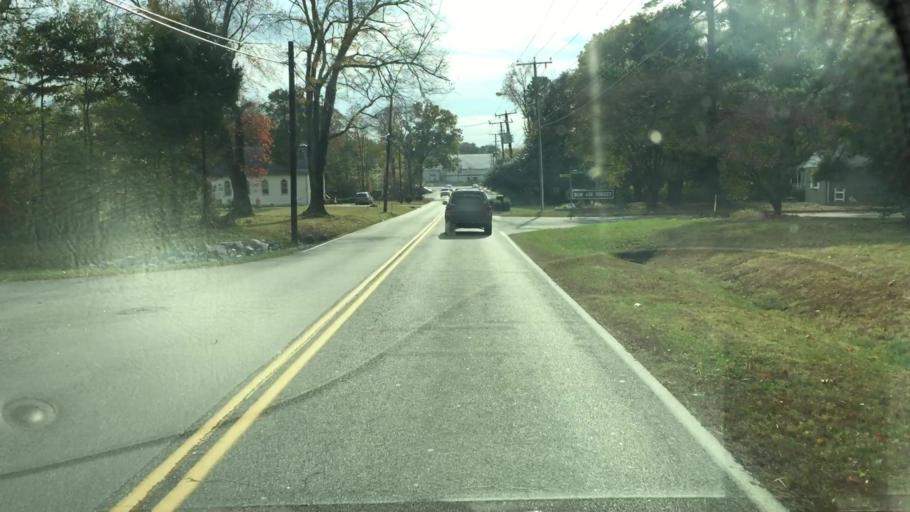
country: US
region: Virginia
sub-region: Chesterfield County
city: Bon Air
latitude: 37.5101
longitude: -77.5798
